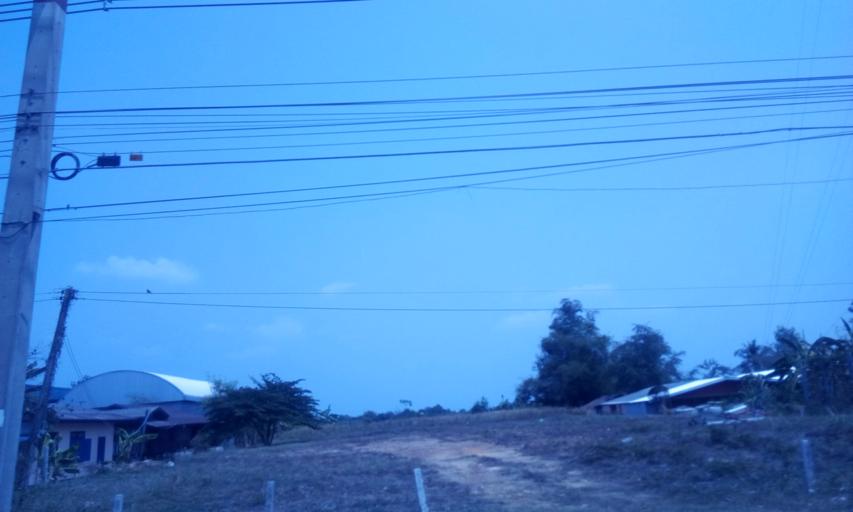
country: TH
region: Chachoengsao
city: Bang Nam Priao
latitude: 13.7748
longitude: 101.0644
